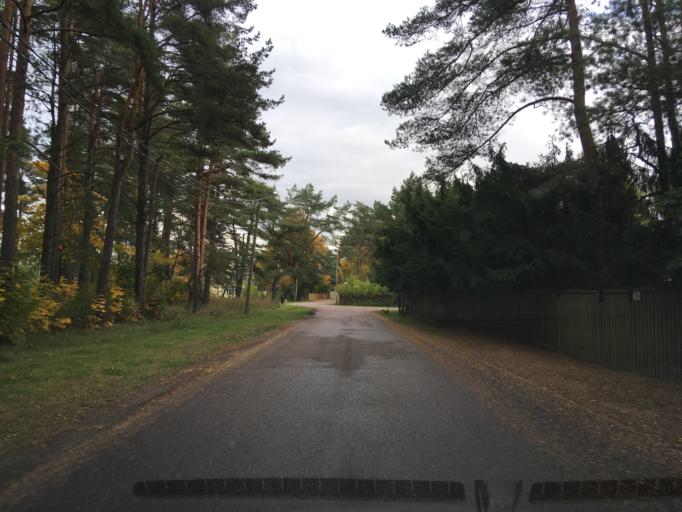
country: EE
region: Harju
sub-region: Tallinna linn
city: Tallinn
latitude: 59.3815
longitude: 24.7135
